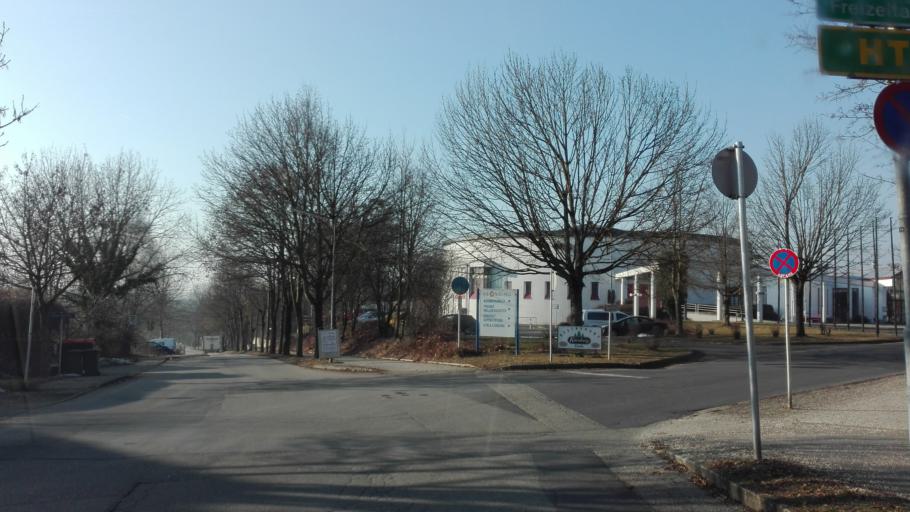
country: AT
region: Upper Austria
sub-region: Politischer Bezirk Linz-Land
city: Leonding
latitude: 48.2658
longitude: 14.2548
